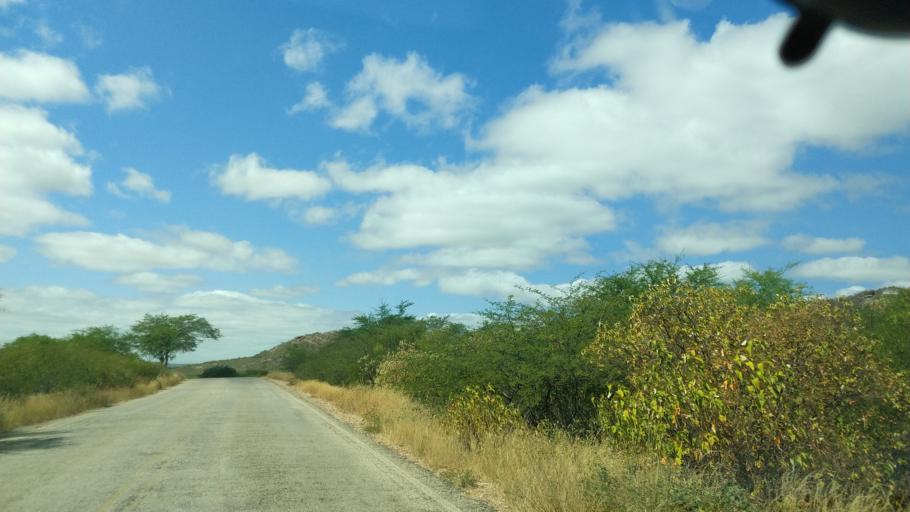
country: BR
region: Rio Grande do Norte
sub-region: Currais Novos
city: Currais Novos
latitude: -6.2624
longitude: -36.5675
